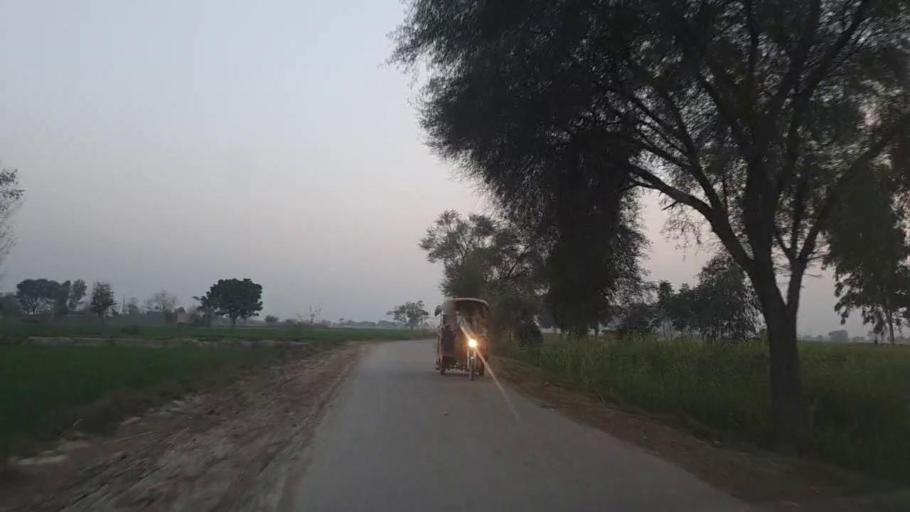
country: PK
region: Sindh
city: Naushahro Firoz
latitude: 26.8648
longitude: 68.0475
